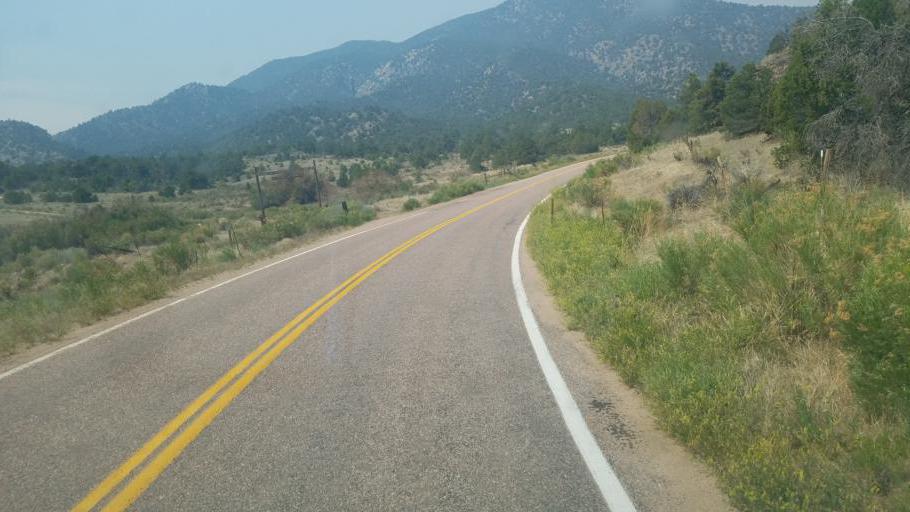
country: US
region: Colorado
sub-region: Fremont County
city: Canon City
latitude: 38.4350
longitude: -105.3809
